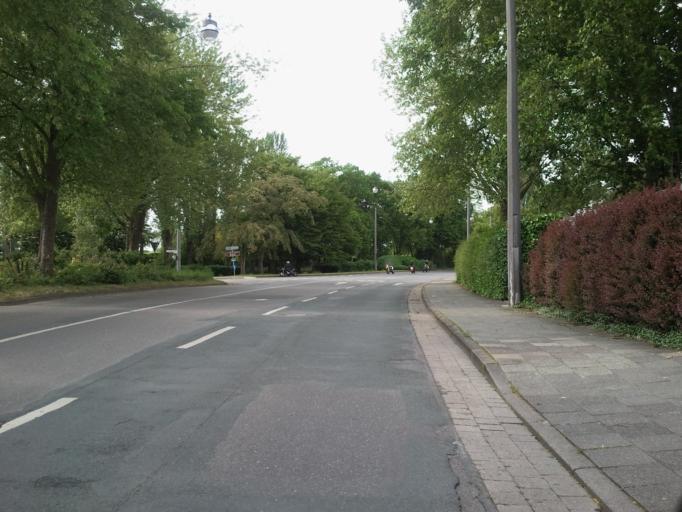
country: DE
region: Lower Saxony
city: Nienburg
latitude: 52.6325
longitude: 9.2081
